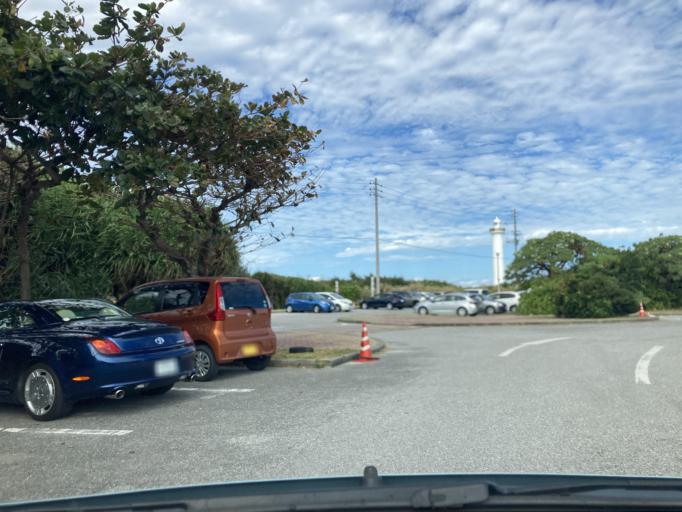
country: JP
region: Okinawa
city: Ishikawa
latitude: 26.4391
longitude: 127.7139
